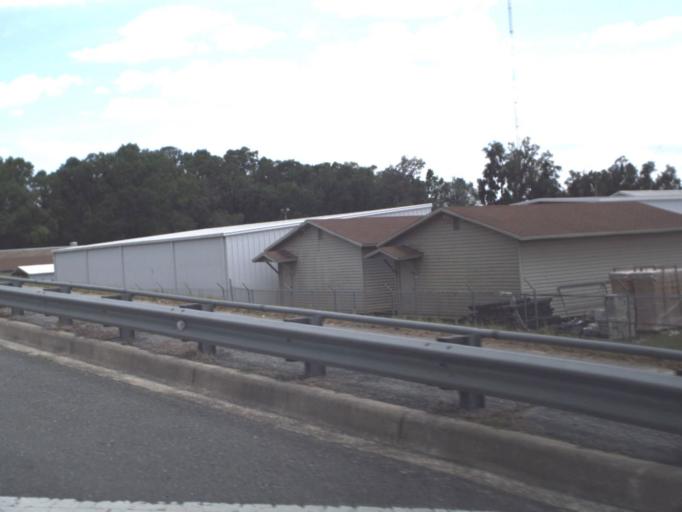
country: US
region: Florida
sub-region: Marion County
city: Ocala
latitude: 29.1789
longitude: -82.1466
